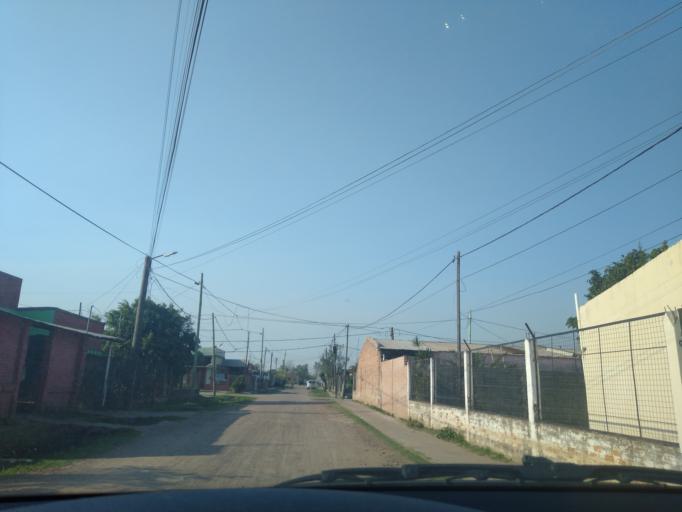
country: AR
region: Chaco
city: Barranqueras
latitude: -27.4704
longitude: -58.9325
